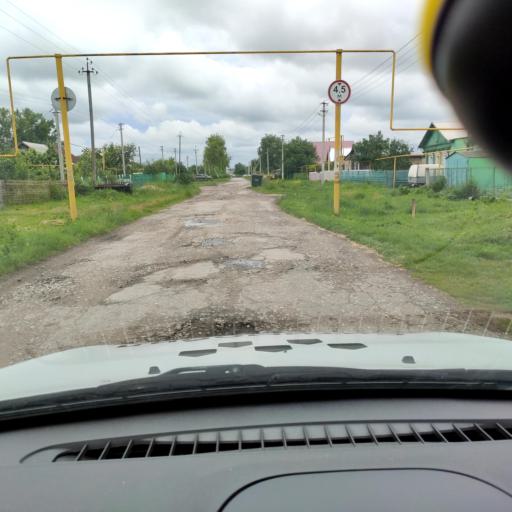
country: RU
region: Samara
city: Tol'yatti
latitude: 53.6484
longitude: 49.3006
